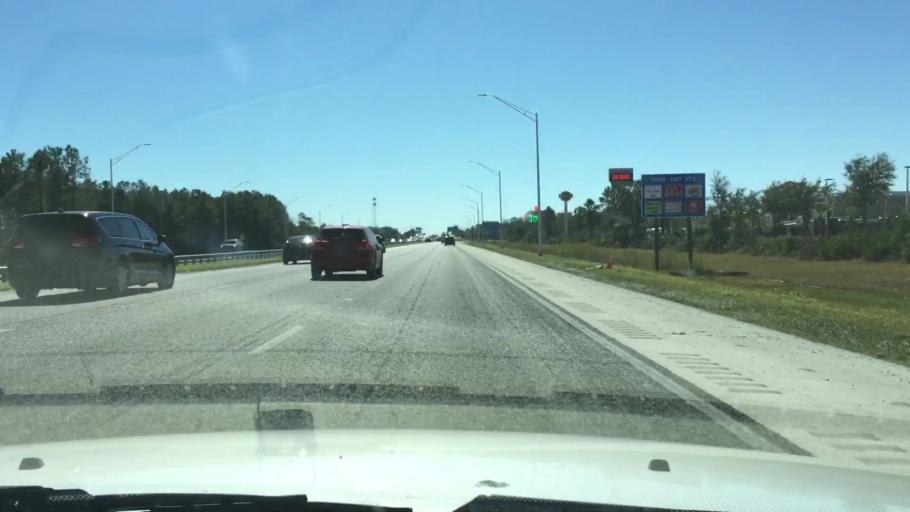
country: US
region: Florida
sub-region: Volusia County
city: Ormond-by-the-Sea
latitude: 29.3452
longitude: -81.1314
